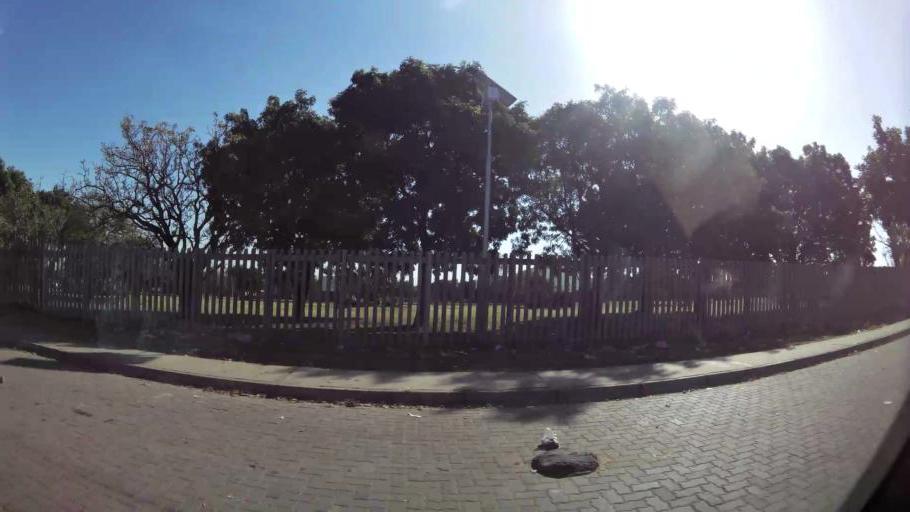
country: ZA
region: Gauteng
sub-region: City of Tshwane Metropolitan Municipality
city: Mabopane
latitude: -25.5430
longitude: 28.0972
